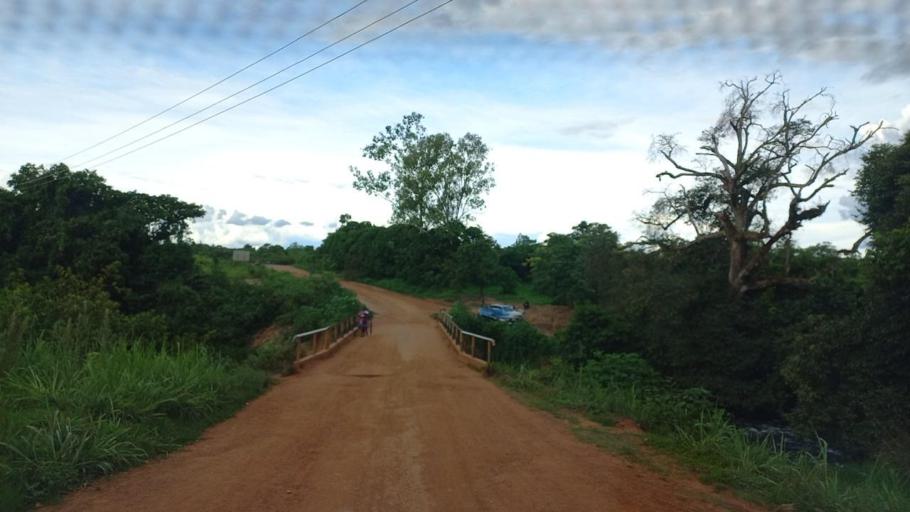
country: ZM
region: North-Western
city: Mwinilunga
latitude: -11.7543
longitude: 24.4363
